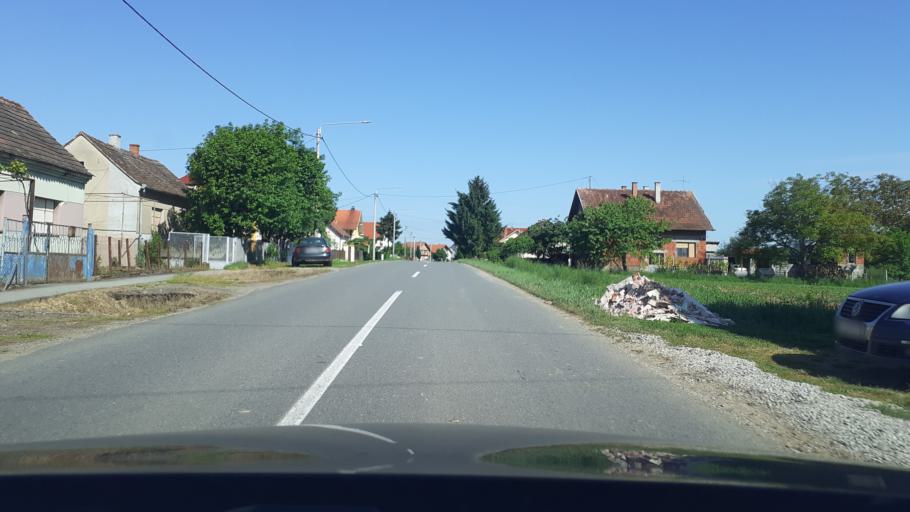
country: HR
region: Pozesko-Slavonska
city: Jaksic
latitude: 45.3383
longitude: 17.7588
